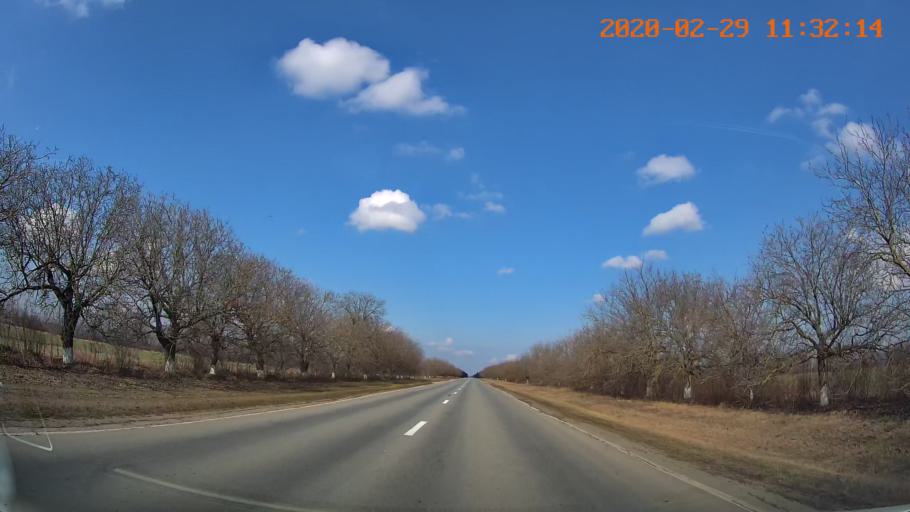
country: MD
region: Rezina
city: Saharna
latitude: 47.5350
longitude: 29.0966
